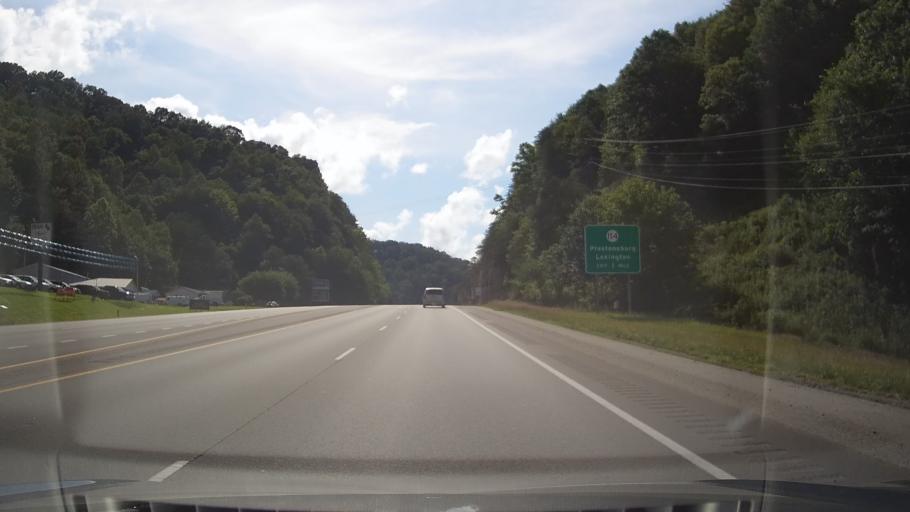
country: US
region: Kentucky
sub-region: Floyd County
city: Prestonsburg
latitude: 37.6436
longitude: -82.7693
